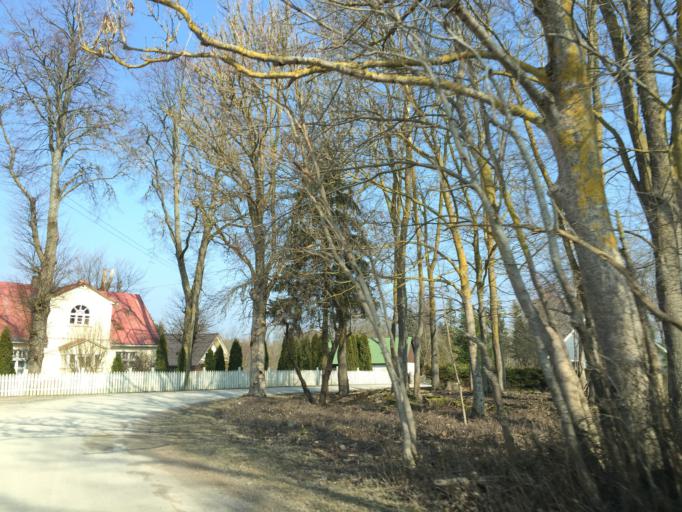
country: EE
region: Saare
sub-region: Kuressaare linn
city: Kuressaare
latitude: 58.3805
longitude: 22.6910
